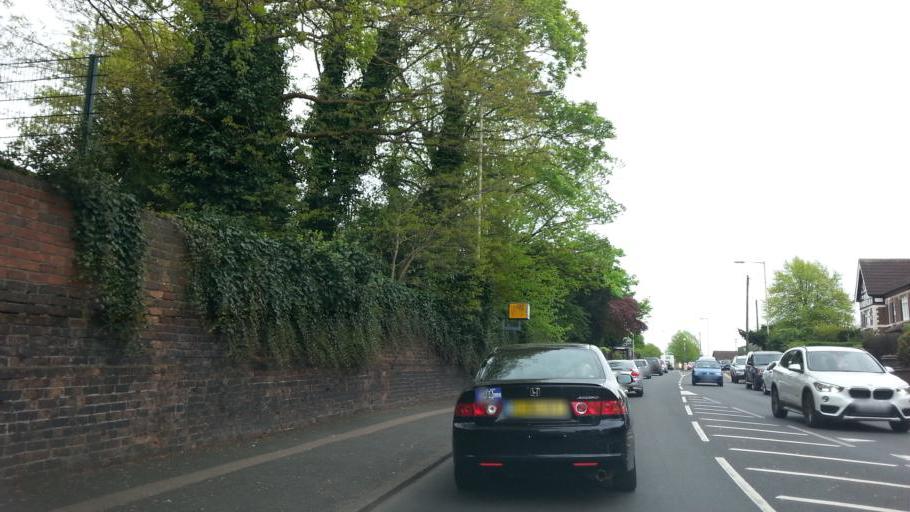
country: GB
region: England
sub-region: Dudley
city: Stourbridge
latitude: 52.4660
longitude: -2.1509
